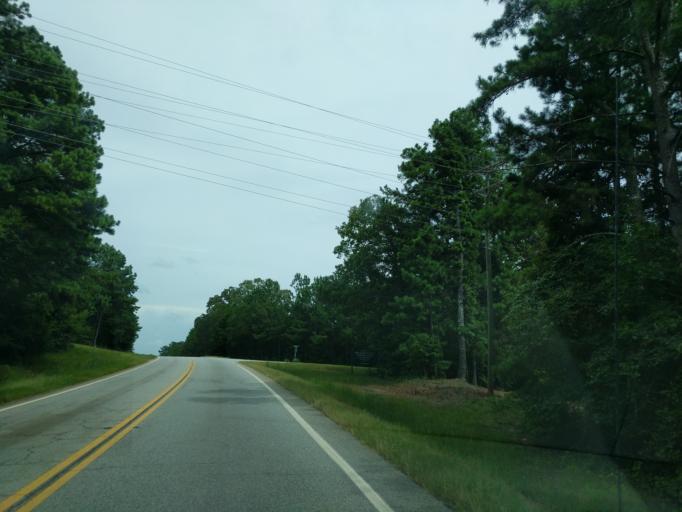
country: US
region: South Carolina
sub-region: Abbeville County
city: Calhoun Falls
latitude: 34.0634
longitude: -82.7284
